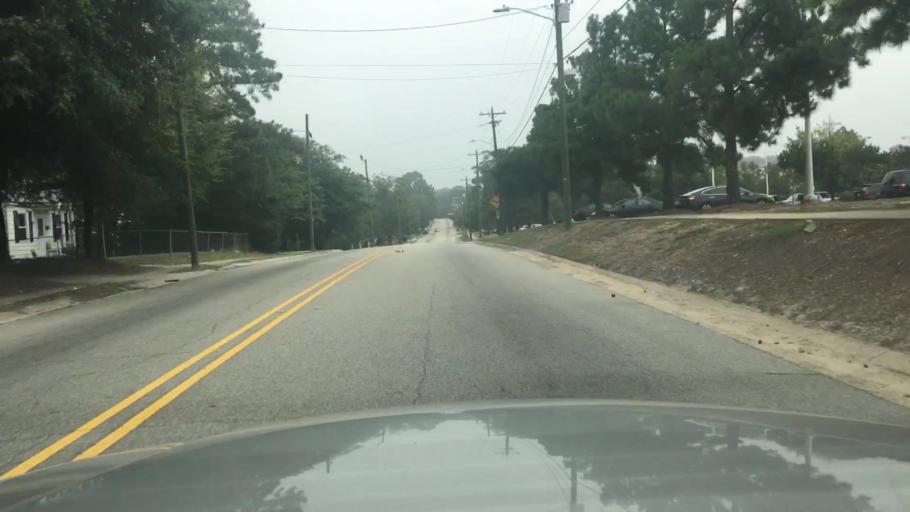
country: US
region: North Carolina
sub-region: Cumberland County
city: Fayetteville
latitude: 35.0715
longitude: -78.8836
